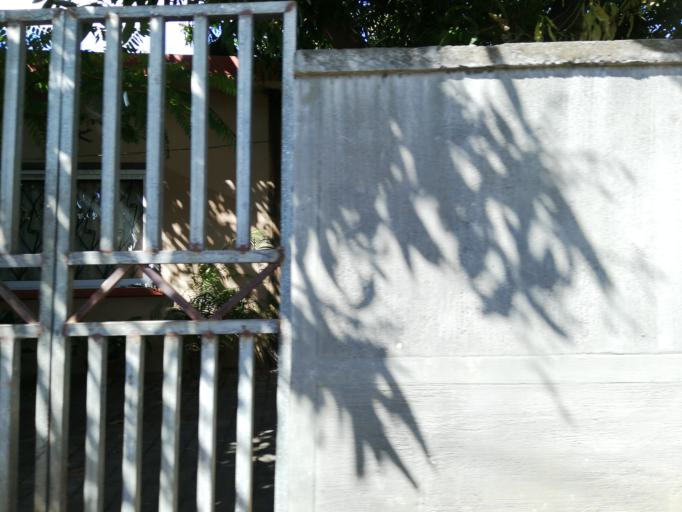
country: MU
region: Moka
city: Moka
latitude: -20.2159
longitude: 57.4674
